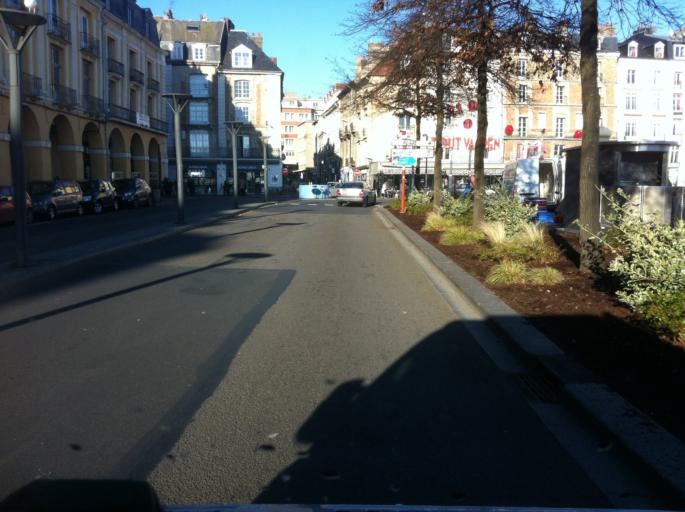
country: FR
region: Haute-Normandie
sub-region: Departement de la Seine-Maritime
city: Dieppe
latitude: 49.9269
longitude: 1.0796
